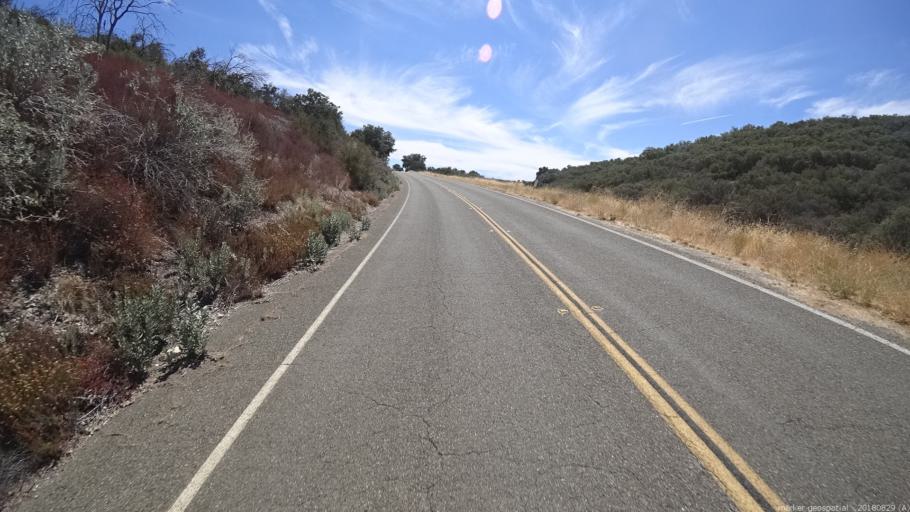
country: US
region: California
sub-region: San Luis Obispo County
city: Lake Nacimiento
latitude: 35.8515
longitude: -121.0538
